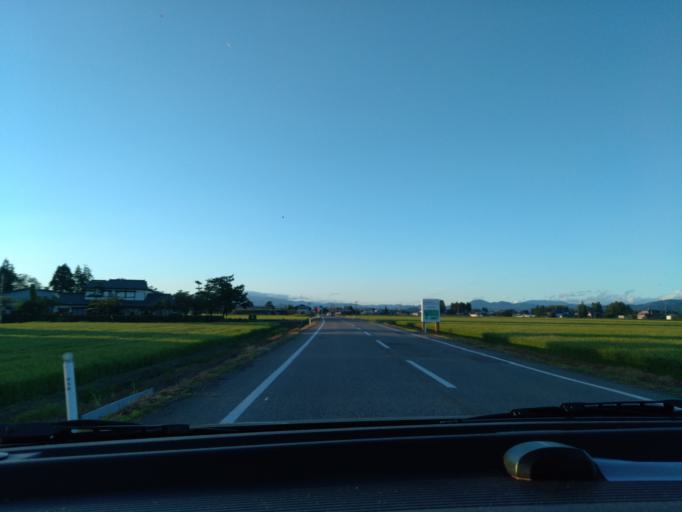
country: JP
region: Akita
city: Omagari
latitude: 39.4965
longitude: 140.5597
